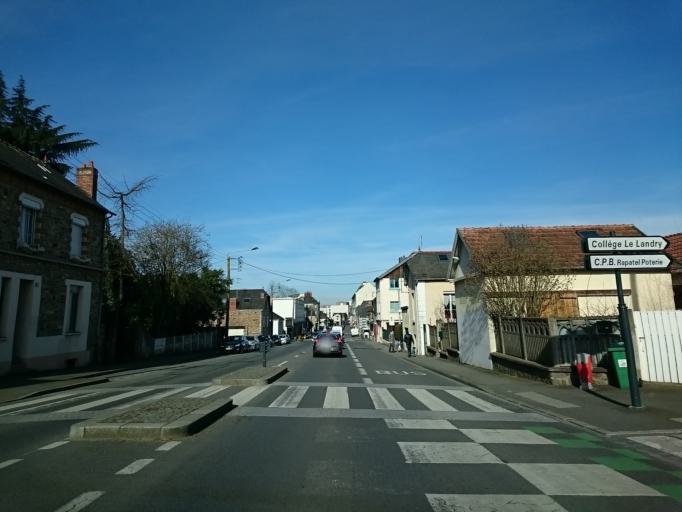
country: FR
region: Brittany
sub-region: Departement d'Ille-et-Vilaine
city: Rennes
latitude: 48.0965
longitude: -1.6527
